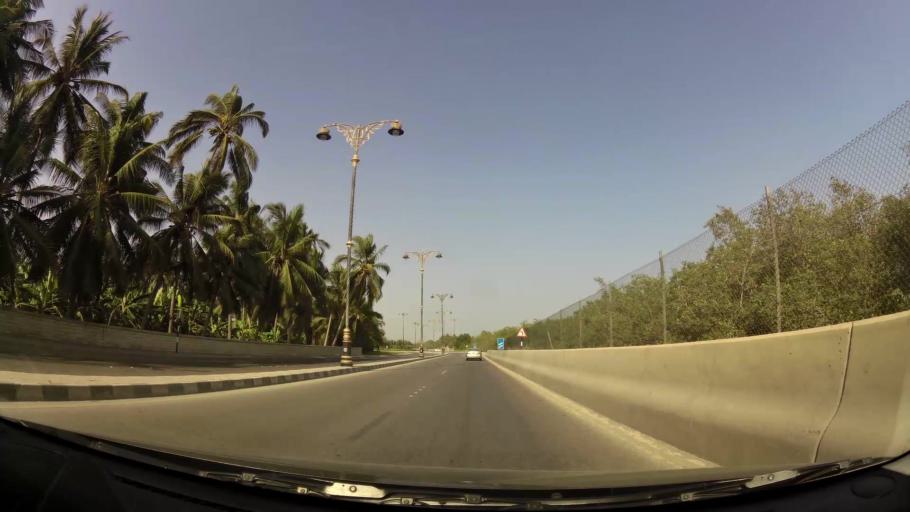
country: OM
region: Zufar
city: Salalah
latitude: 16.9983
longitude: 54.0732
